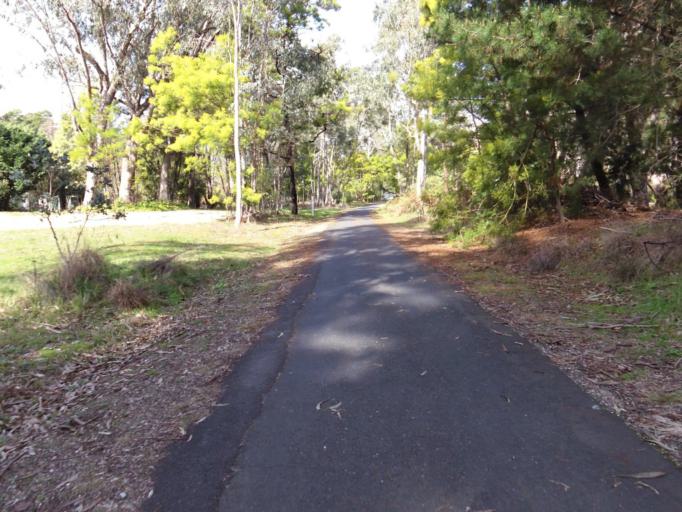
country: AU
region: Victoria
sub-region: Alpine
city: Mount Beauty
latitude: -36.7167
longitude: 146.9430
